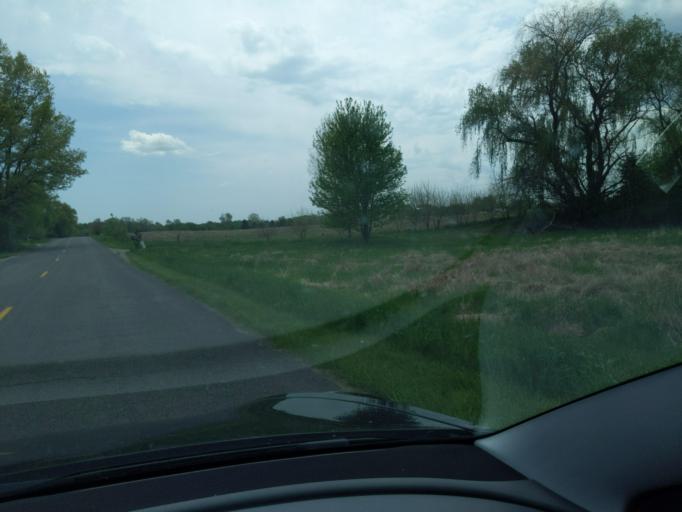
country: US
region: Michigan
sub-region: Ingham County
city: Stockbridge
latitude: 42.4508
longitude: -84.2246
